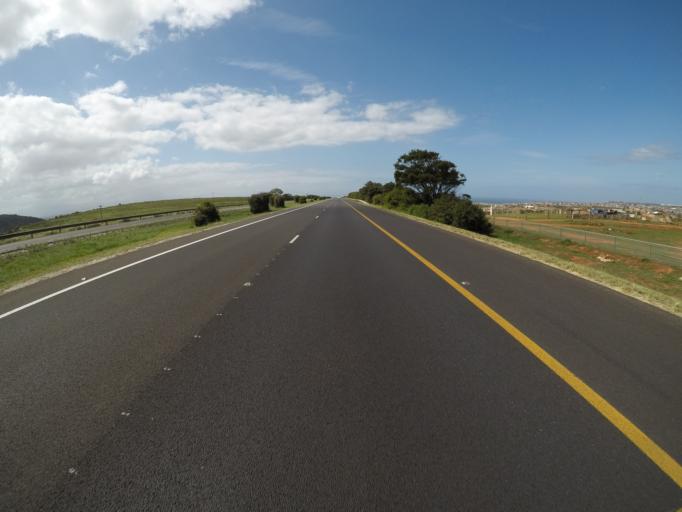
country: ZA
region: Western Cape
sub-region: Eden District Municipality
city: Mossel Bay
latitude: -34.1661
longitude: 22.0851
